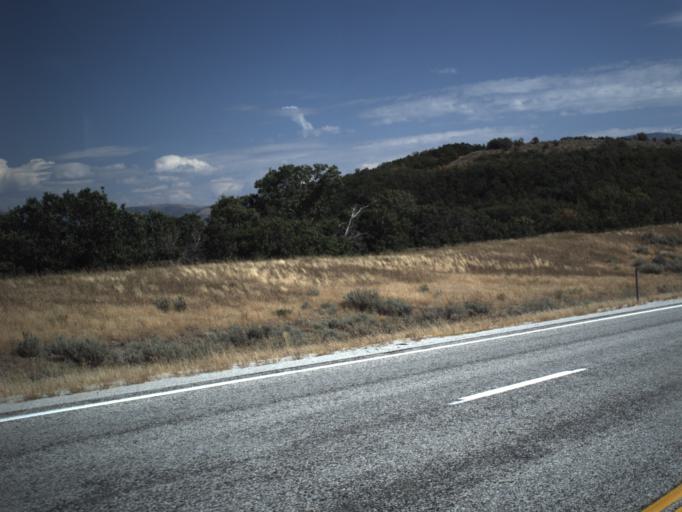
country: US
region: Utah
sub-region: Morgan County
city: Mountain Green
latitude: 41.1856
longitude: -111.8095
